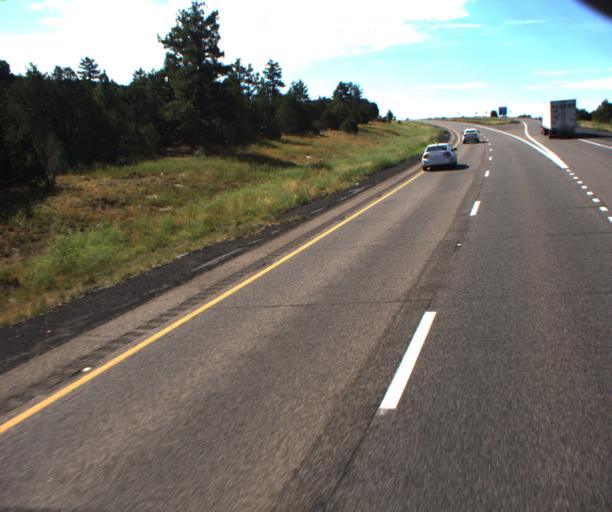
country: US
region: Arizona
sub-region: Yavapai County
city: Village of Oak Creek (Big Park)
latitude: 34.8160
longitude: -111.6130
